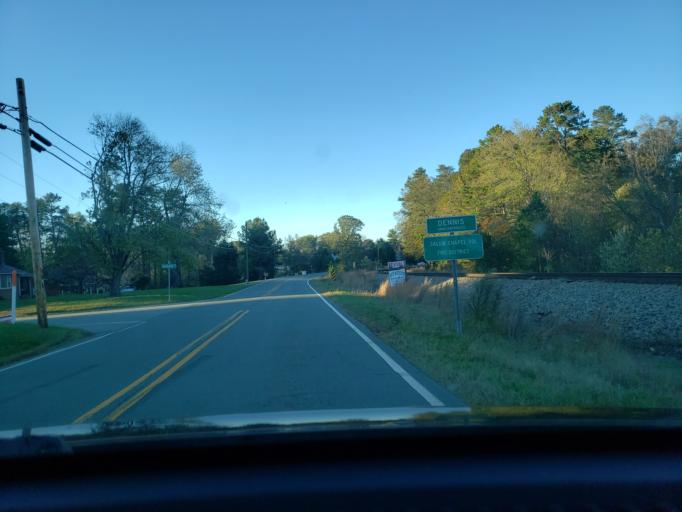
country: US
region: North Carolina
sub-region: Forsyth County
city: Walkertown
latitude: 36.2238
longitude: -80.1691
